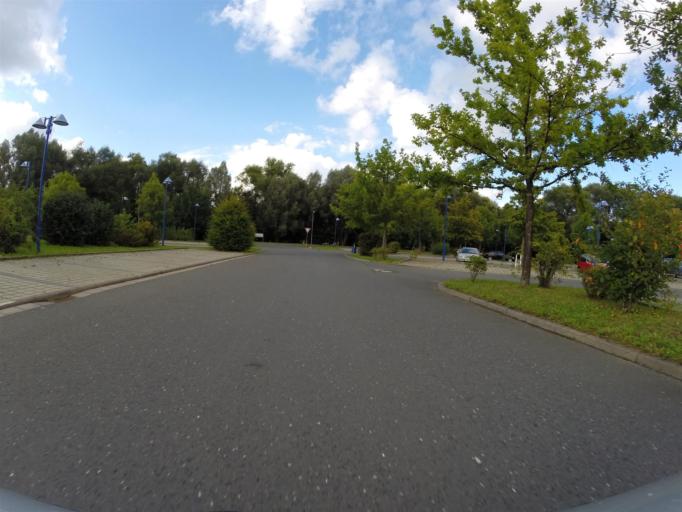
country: DE
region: Thuringia
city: Jena
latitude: 50.9008
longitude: 11.5931
